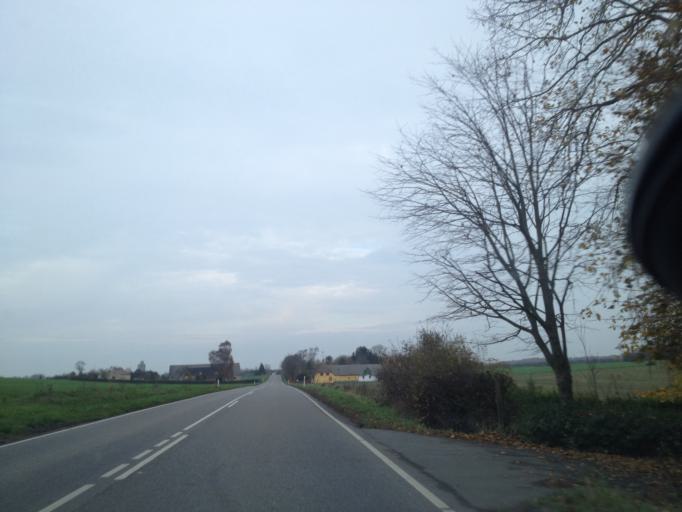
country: DK
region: South Denmark
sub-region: Nordfyns Kommune
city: Bogense
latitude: 55.5131
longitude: 10.0995
